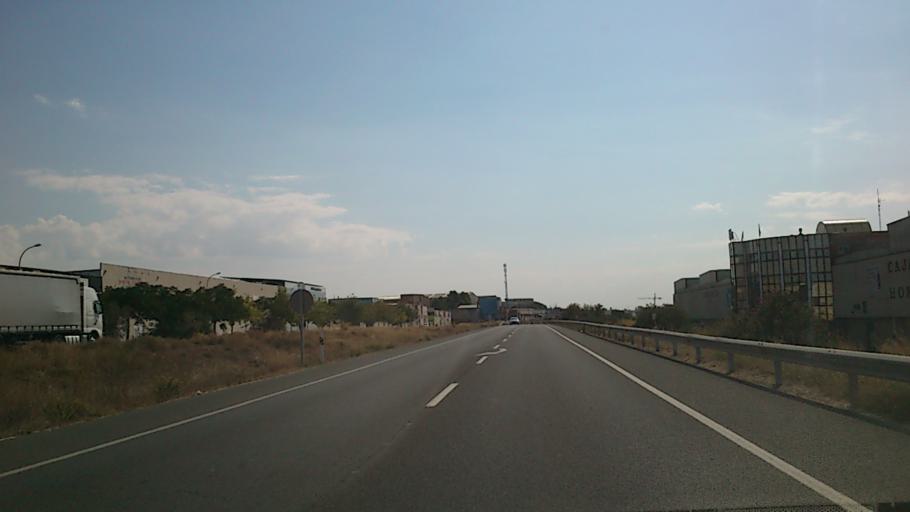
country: ES
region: Aragon
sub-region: Provincia de Zaragoza
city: Puebla de Alfinden
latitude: 41.6409
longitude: -0.7688
